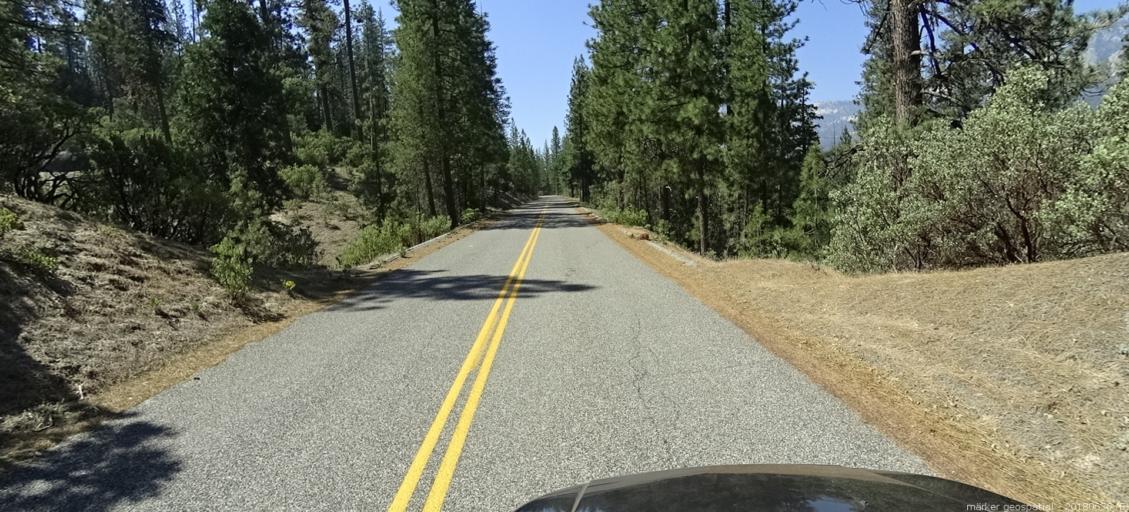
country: US
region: California
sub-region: Madera County
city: Oakhurst
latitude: 37.3797
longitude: -119.3808
